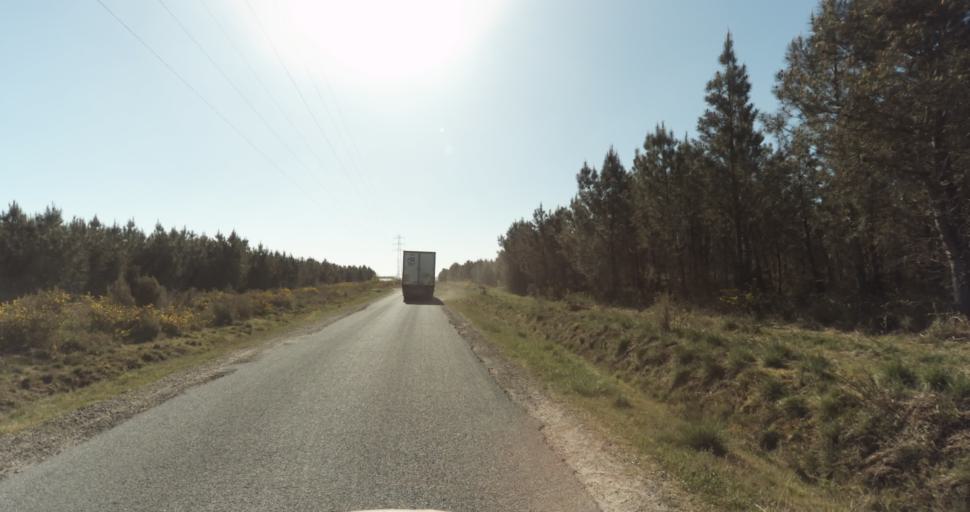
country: FR
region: Aquitaine
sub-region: Departement de la Gironde
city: Marcheprime
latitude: 44.7493
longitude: -0.8446
